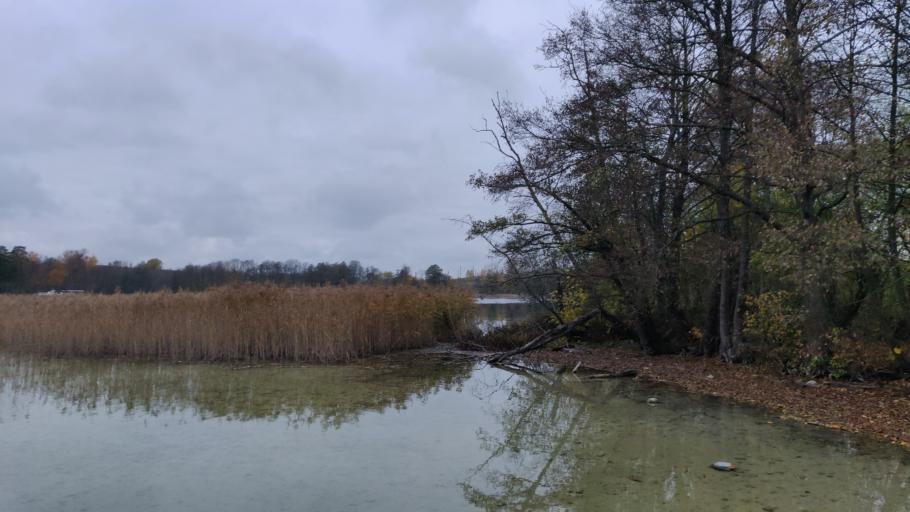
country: LT
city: Trakai
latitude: 54.6694
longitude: 24.9363
